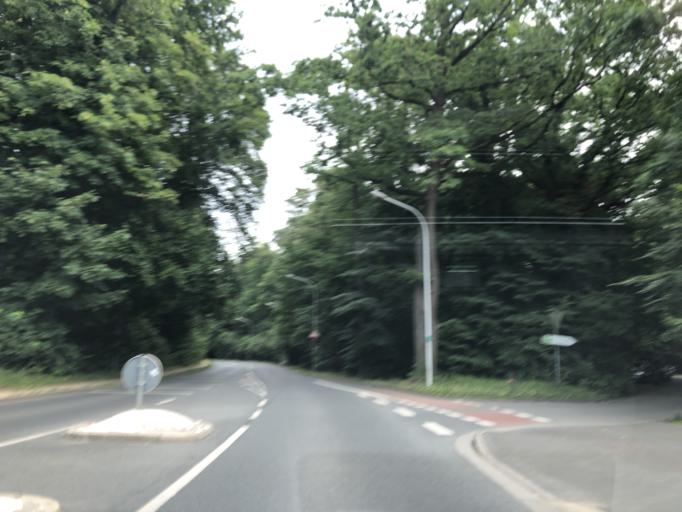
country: DE
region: Hesse
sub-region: Regierungsbezirk Darmstadt
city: Darmstadt
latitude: 49.8511
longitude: 8.6624
